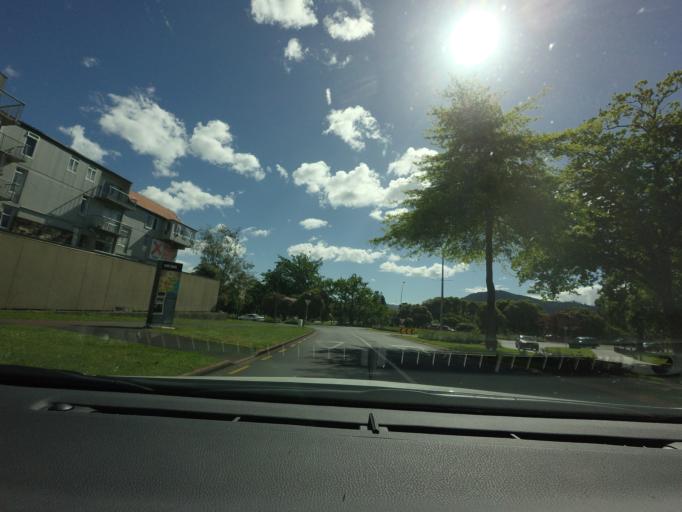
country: NZ
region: Bay of Plenty
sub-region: Rotorua District
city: Rotorua
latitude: -38.1349
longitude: 176.2476
